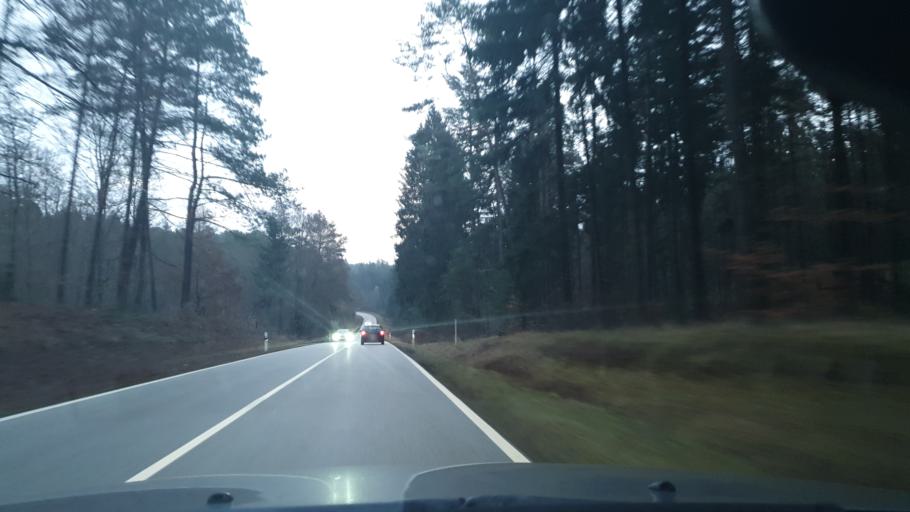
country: DE
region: Rheinland-Pfalz
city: Krickenbach
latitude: 49.3844
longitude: 7.6601
